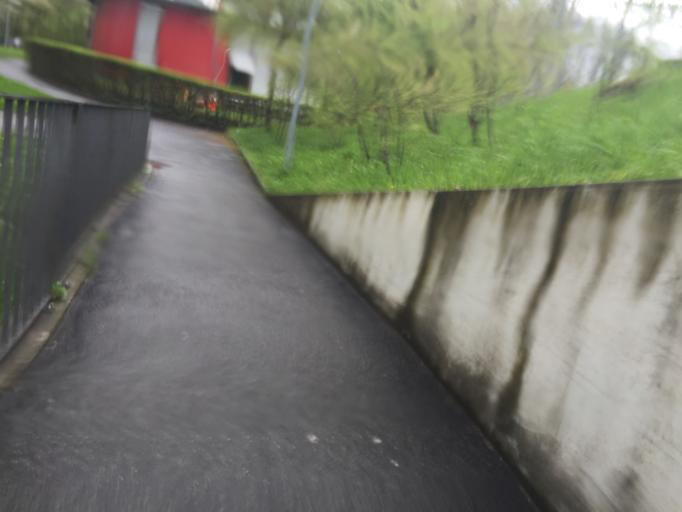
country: CH
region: Bern
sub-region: Bern-Mittelland District
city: Zollikofen
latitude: 46.9810
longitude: 7.4593
